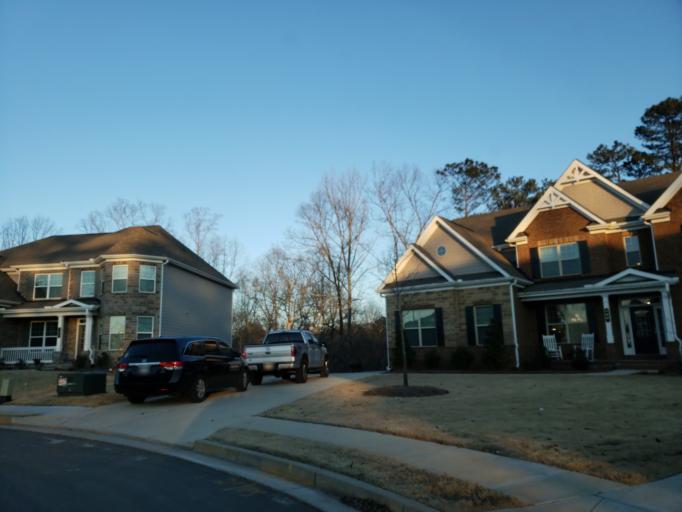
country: US
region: Georgia
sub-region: Cherokee County
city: Woodstock
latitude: 34.1149
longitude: -84.4524
